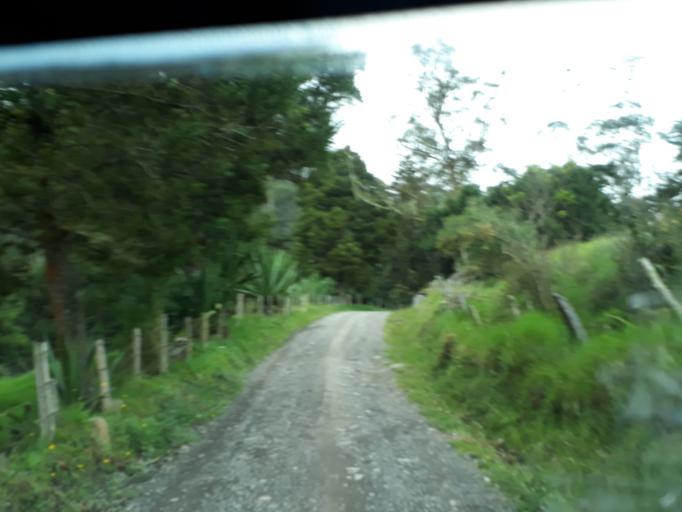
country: CO
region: Cundinamarca
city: Carmen de Carupa
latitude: 5.3791
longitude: -73.9784
